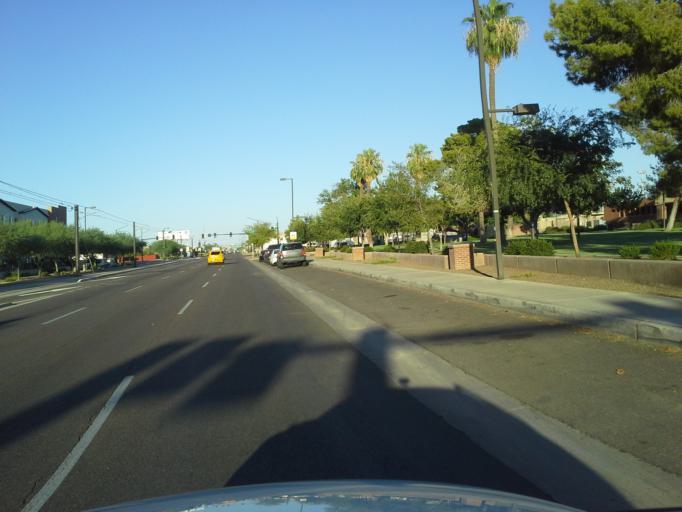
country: US
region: Arizona
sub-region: Maricopa County
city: Phoenix
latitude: 33.4472
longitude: -112.0496
